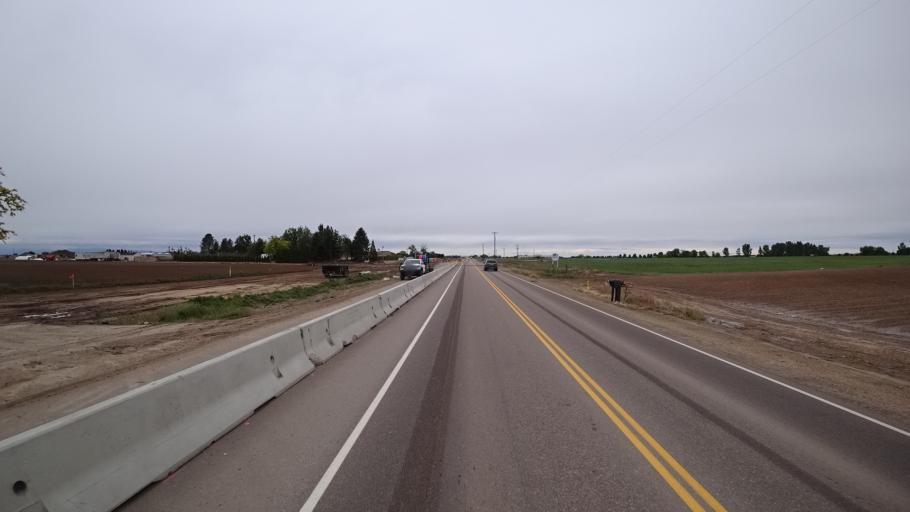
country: US
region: Idaho
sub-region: Ada County
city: Star
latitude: 43.6630
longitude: -116.4597
